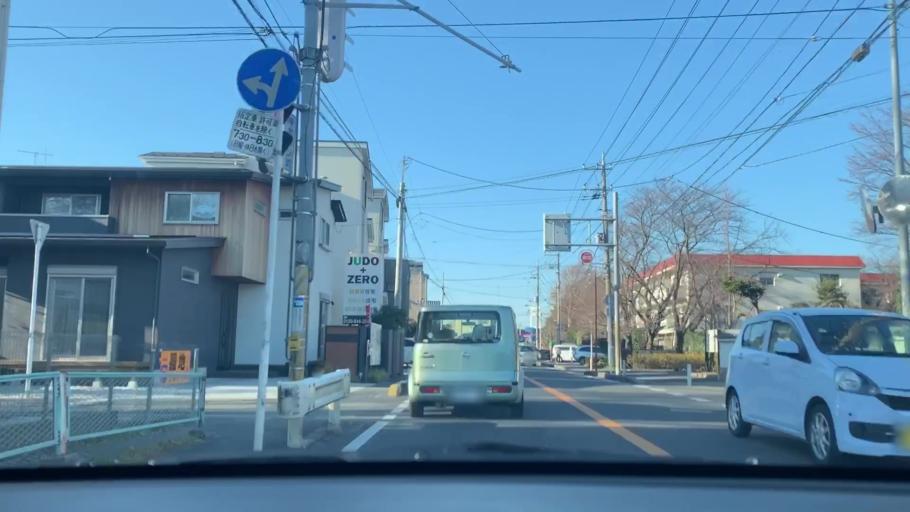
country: JP
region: Chiba
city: Matsudo
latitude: 35.7531
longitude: 139.9013
